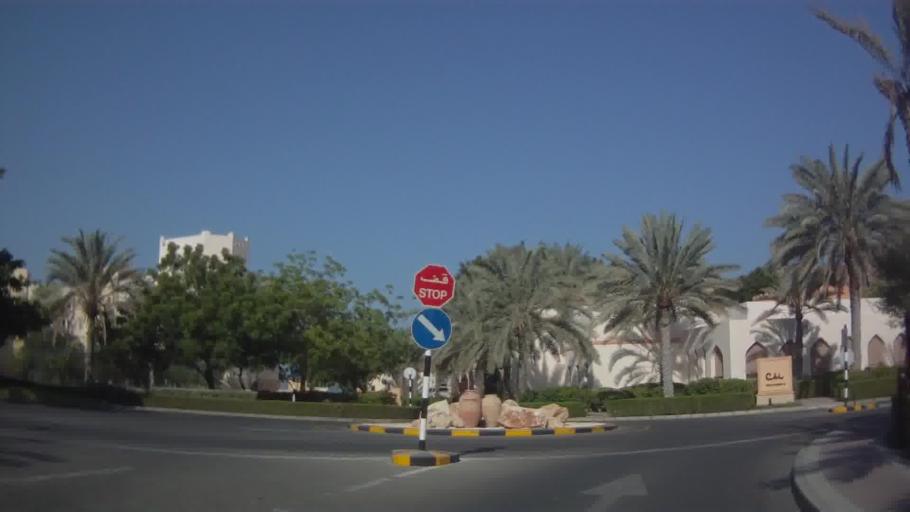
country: OM
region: Muhafazat Masqat
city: Muscat
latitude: 23.5487
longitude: 58.6604
